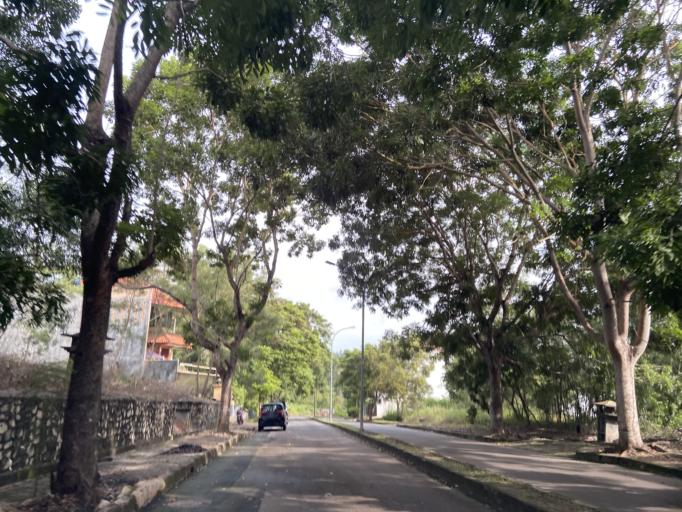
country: SG
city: Singapore
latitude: 1.1002
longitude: 104.0275
